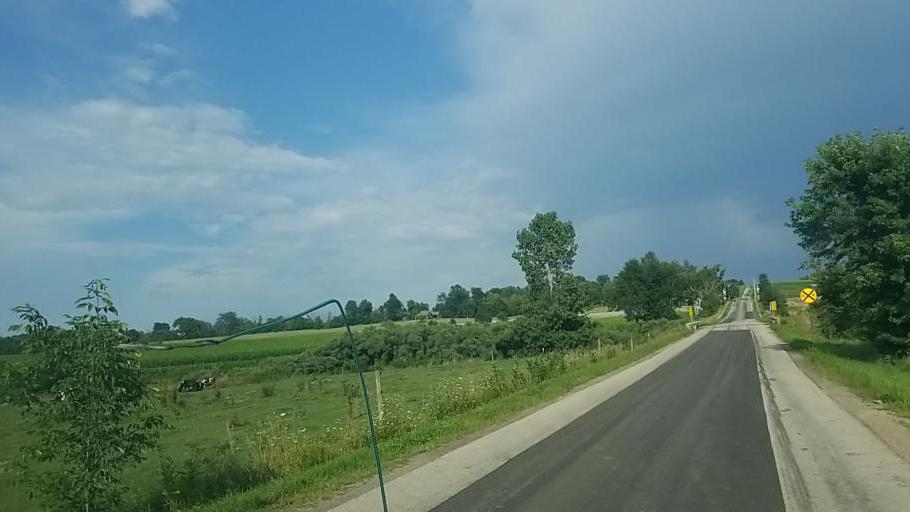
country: US
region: Ohio
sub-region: Wayne County
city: Smithville
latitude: 40.9163
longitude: -81.8753
